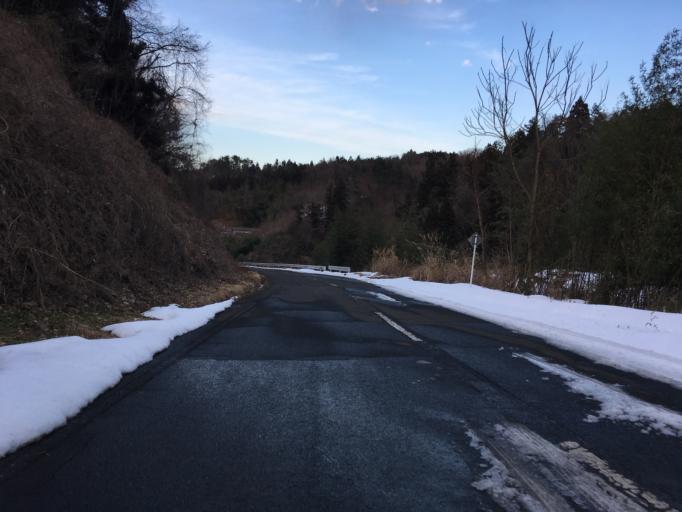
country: JP
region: Fukushima
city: Fukushima-shi
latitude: 37.6389
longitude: 140.5879
